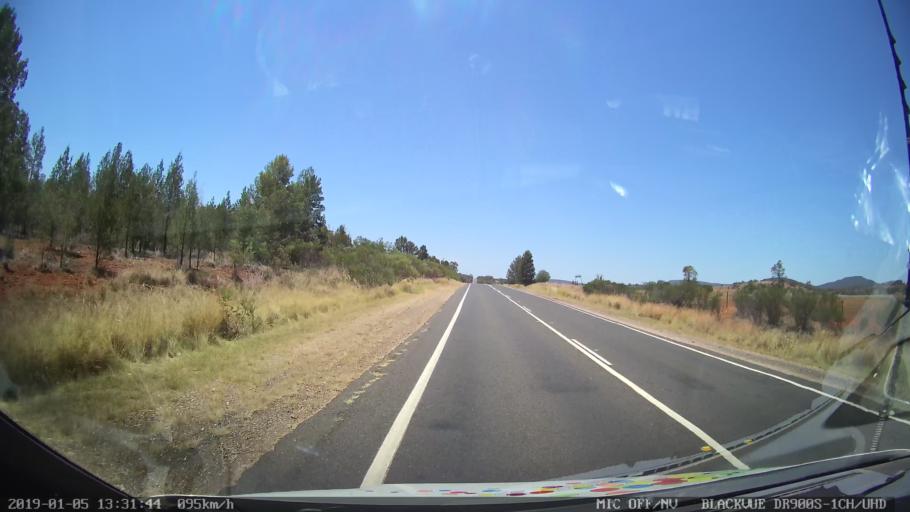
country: AU
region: New South Wales
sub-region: Gunnedah
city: Gunnedah
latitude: -31.0092
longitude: 150.0886
